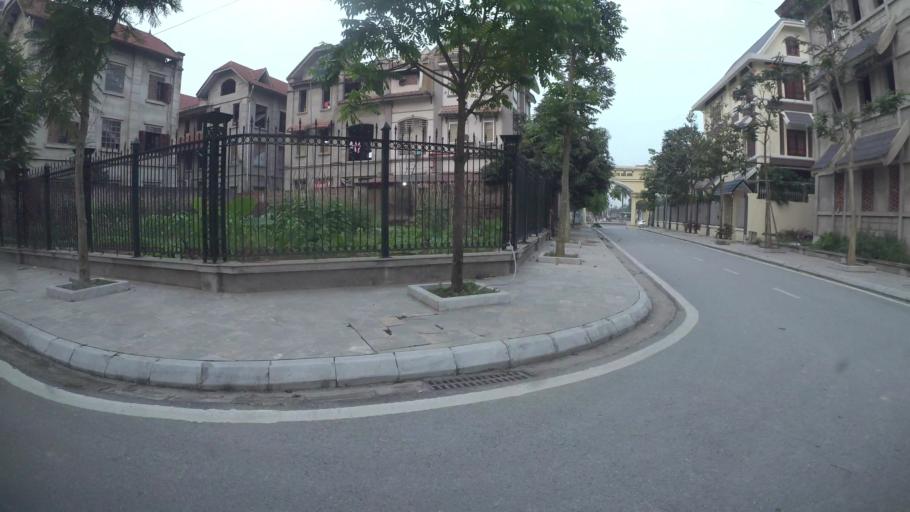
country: VN
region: Ha Noi
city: Cau Dien
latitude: 21.0013
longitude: 105.7325
